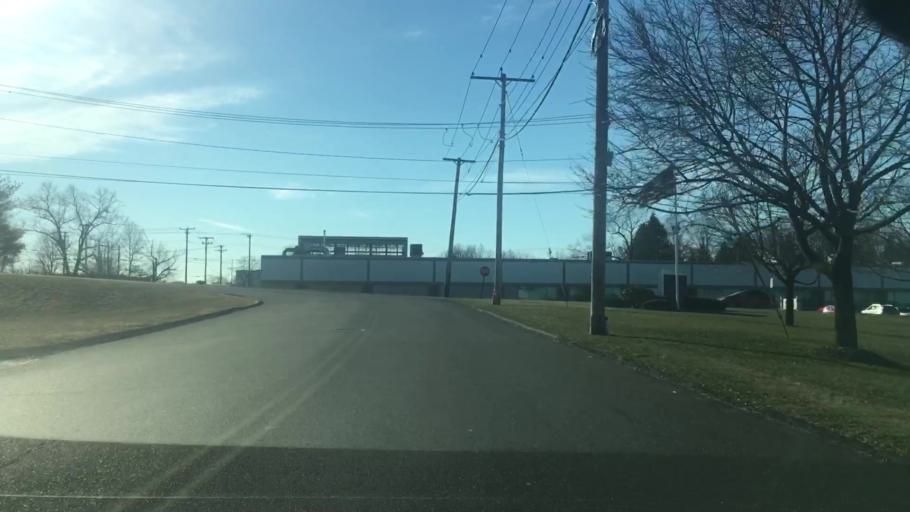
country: US
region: Connecticut
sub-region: New Haven County
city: North Haven
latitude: 41.4191
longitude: -72.8447
